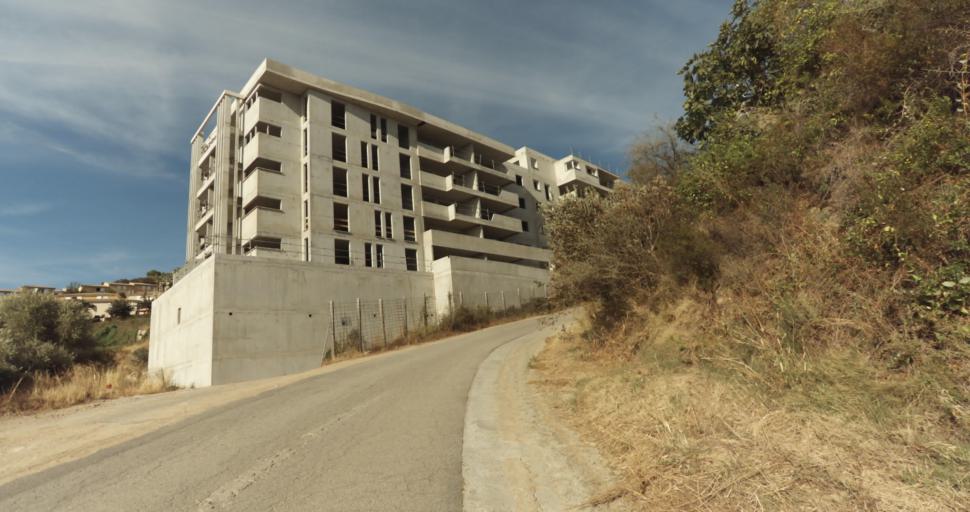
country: FR
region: Corsica
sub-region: Departement de la Corse-du-Sud
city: Afa
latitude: 41.9338
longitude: 8.7910
